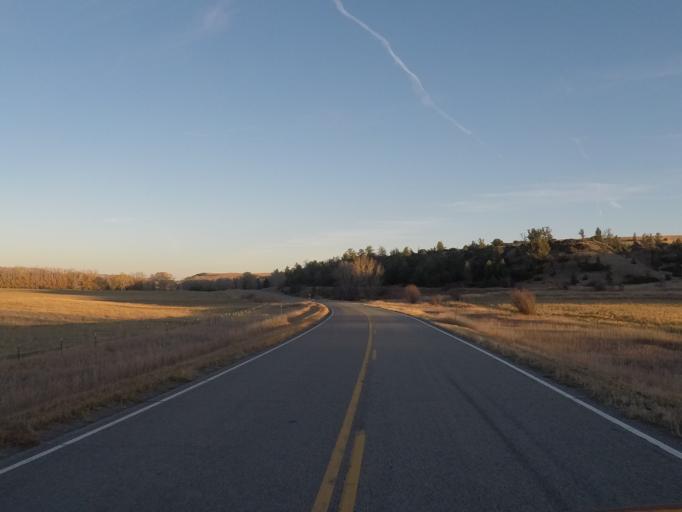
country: US
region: Montana
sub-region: Sweet Grass County
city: Big Timber
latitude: 45.7866
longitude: -109.8491
